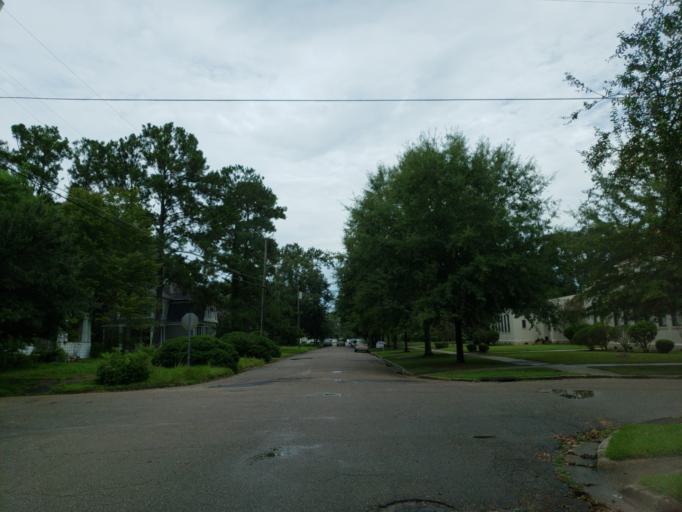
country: US
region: Mississippi
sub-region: Forrest County
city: Hattiesburg
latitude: 31.3193
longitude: -89.2877
